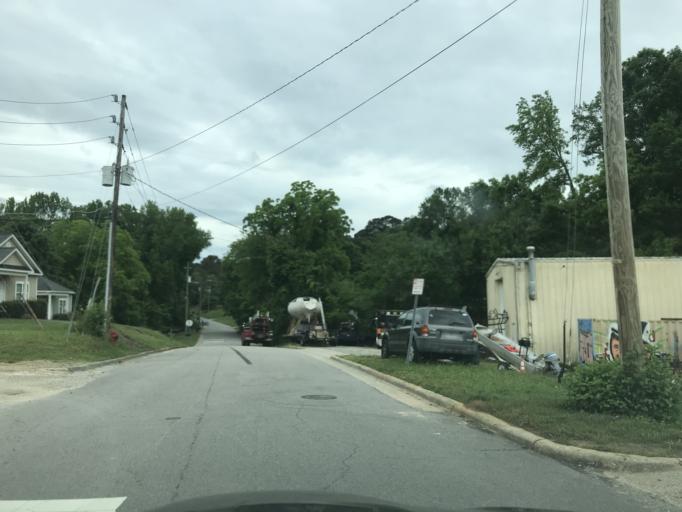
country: US
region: North Carolina
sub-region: Wake County
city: West Raleigh
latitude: 35.7929
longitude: -78.6882
